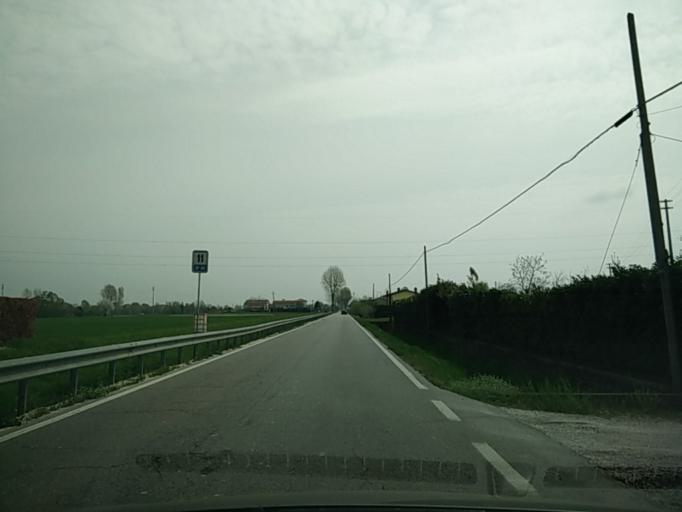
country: IT
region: Veneto
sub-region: Provincia di Venezia
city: Caltana
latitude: 45.4753
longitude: 12.0507
